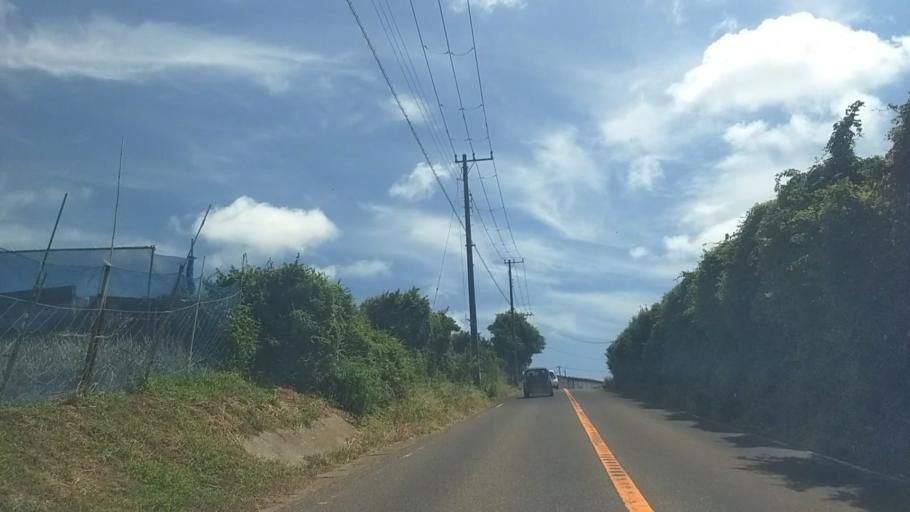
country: JP
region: Kanagawa
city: Miura
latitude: 35.1998
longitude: 139.6511
